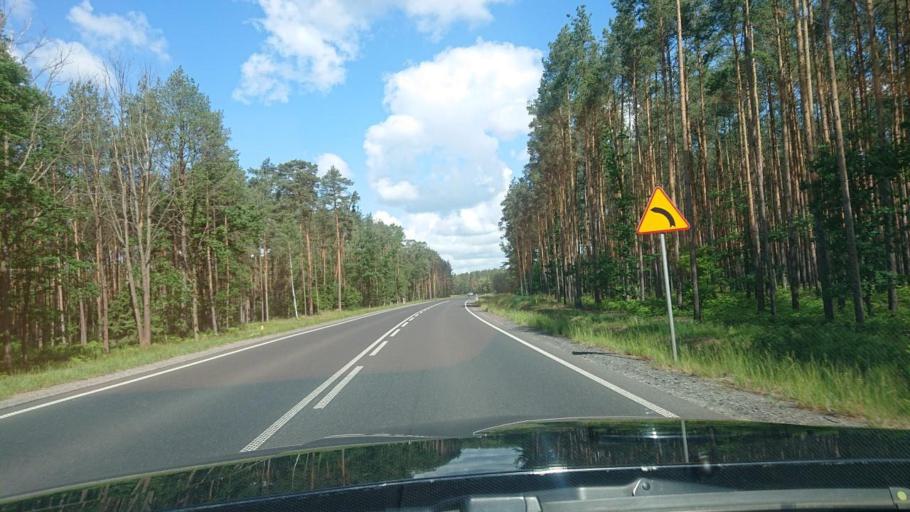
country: PL
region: Lubusz
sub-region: Powiat zaganski
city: Szprotawa
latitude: 51.5371
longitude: 15.6250
